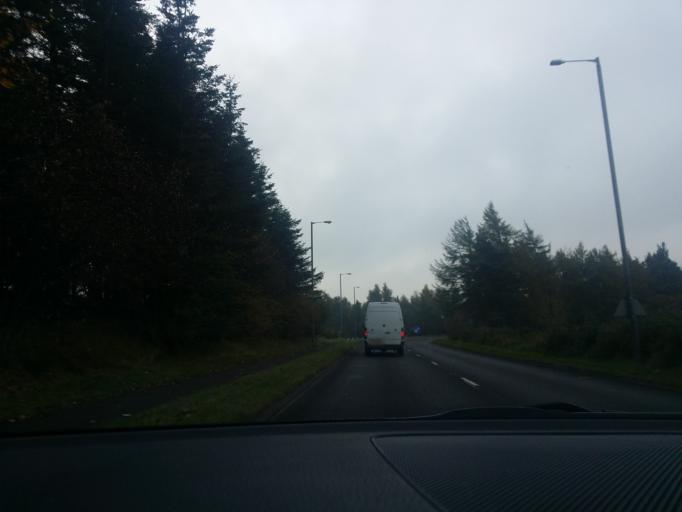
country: GB
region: Scotland
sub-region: Stirling
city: Bannockburn
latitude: 56.0796
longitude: -3.9223
